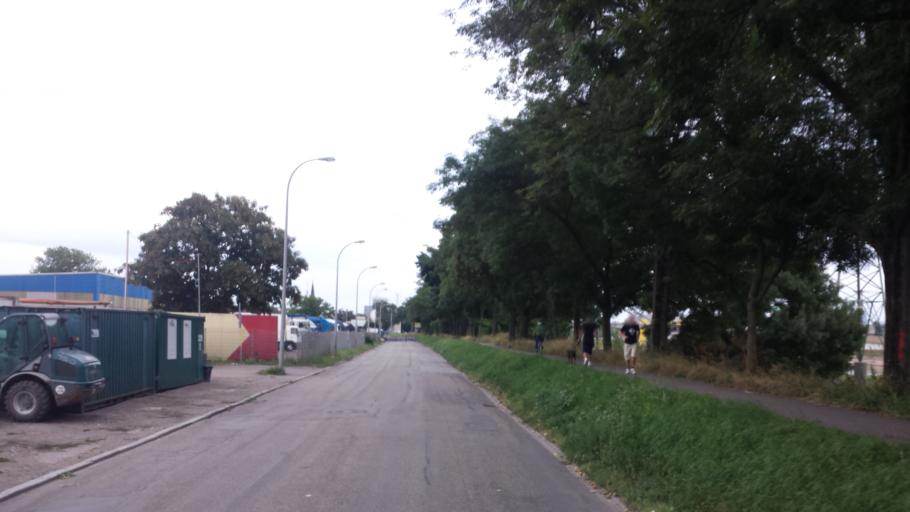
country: DE
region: Rheinland-Pfalz
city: Ludwigshafen am Rhein
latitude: 49.5038
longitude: 8.4516
